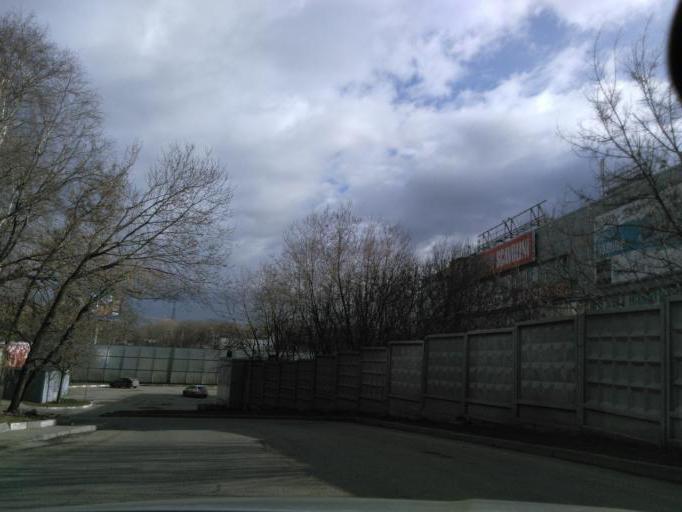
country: RU
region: Moscow
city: Novyye Cheremushki
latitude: 55.7015
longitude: 37.6030
